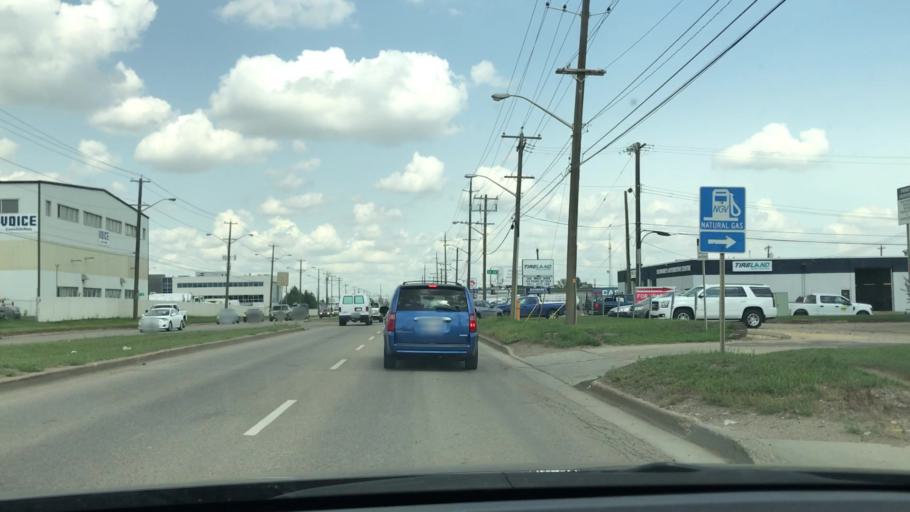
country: CA
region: Alberta
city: Edmonton
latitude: 53.5095
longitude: -113.4183
